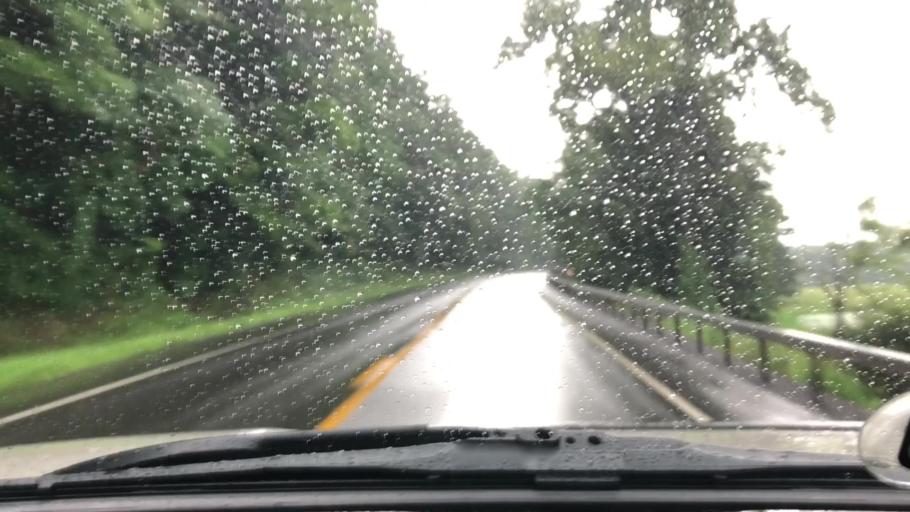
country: US
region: New York
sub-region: Greene County
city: Palenville
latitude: 42.1965
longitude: -73.9860
